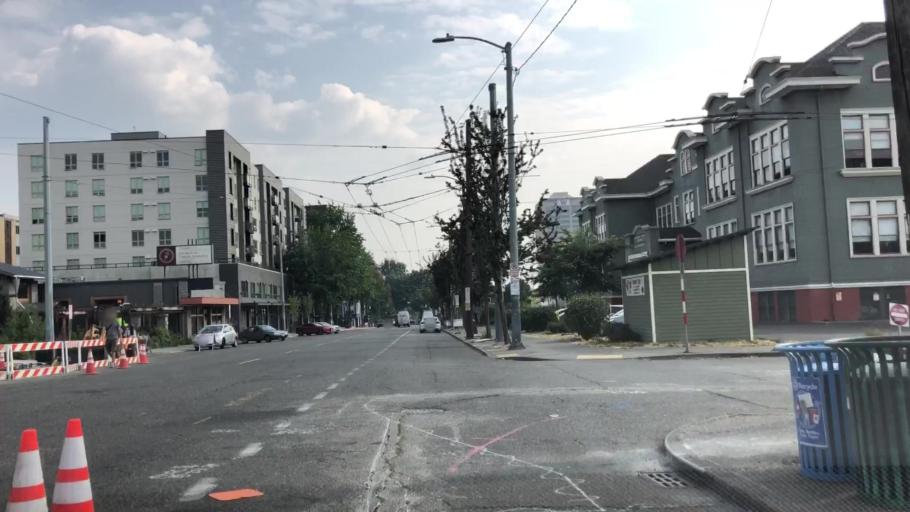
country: US
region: Washington
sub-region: King County
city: Seattle
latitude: 47.6666
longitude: -122.3131
